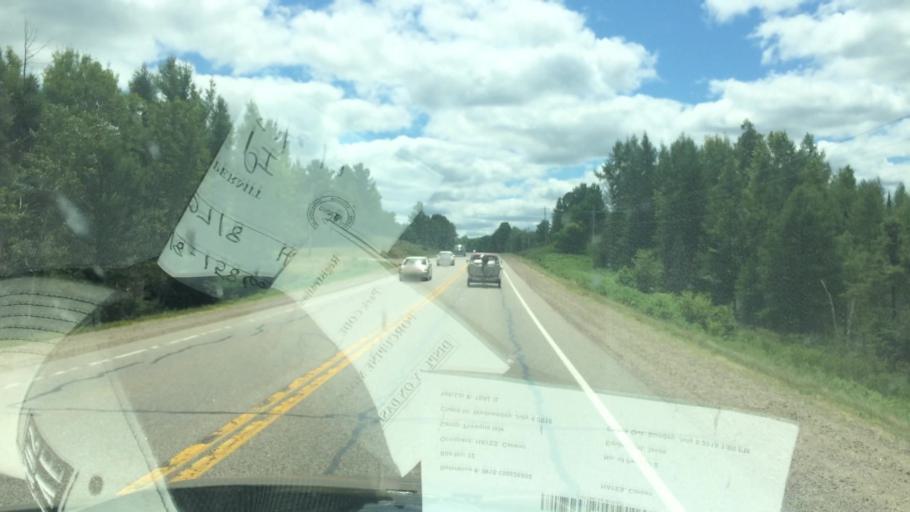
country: US
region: Wisconsin
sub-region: Vilas County
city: Eagle River
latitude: 45.7971
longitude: -89.3203
